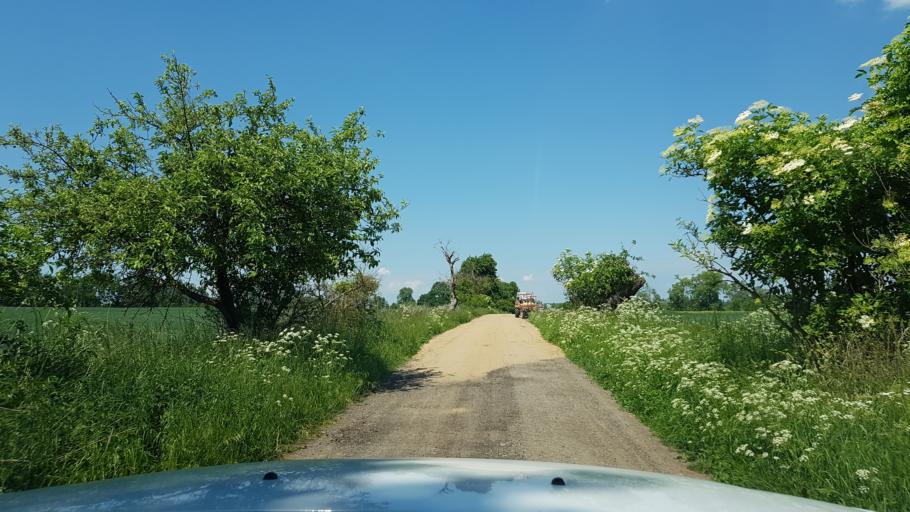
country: PL
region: West Pomeranian Voivodeship
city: Trzcinsko Zdroj
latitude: 52.9479
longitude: 14.5810
